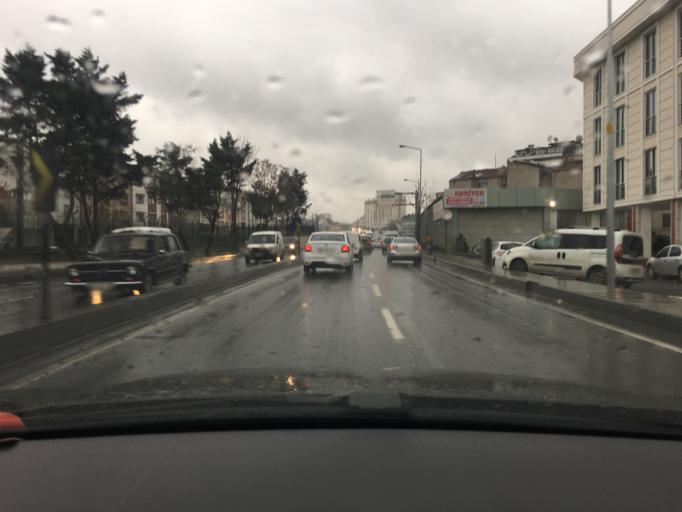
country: TR
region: Istanbul
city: merter keresteciler
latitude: 41.0314
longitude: 28.8975
